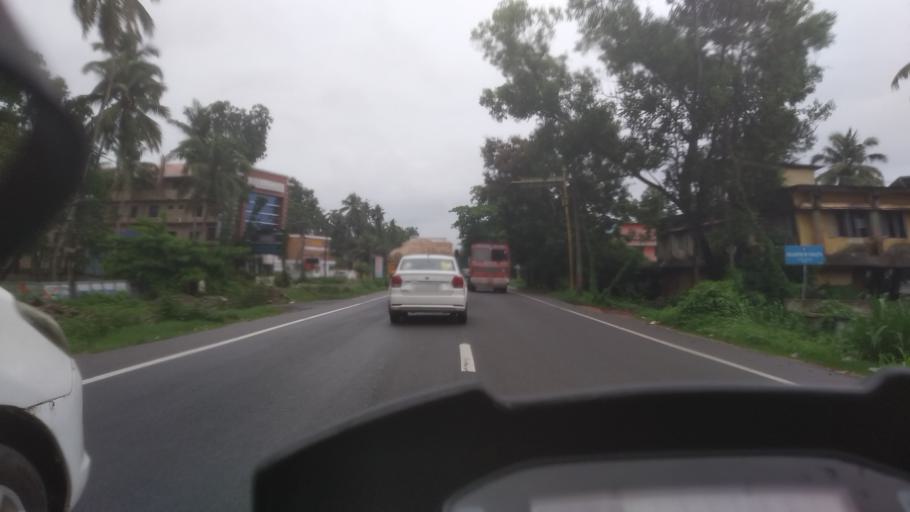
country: IN
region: Kerala
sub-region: Alappuzha
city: Kayankulam
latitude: 9.1663
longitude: 76.5015
